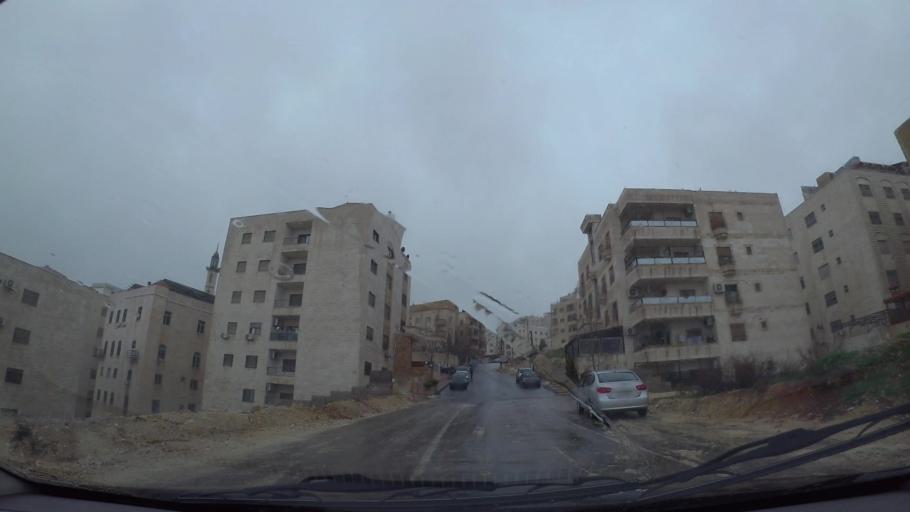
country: JO
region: Amman
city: Al Jubayhah
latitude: 32.0208
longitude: 35.8926
